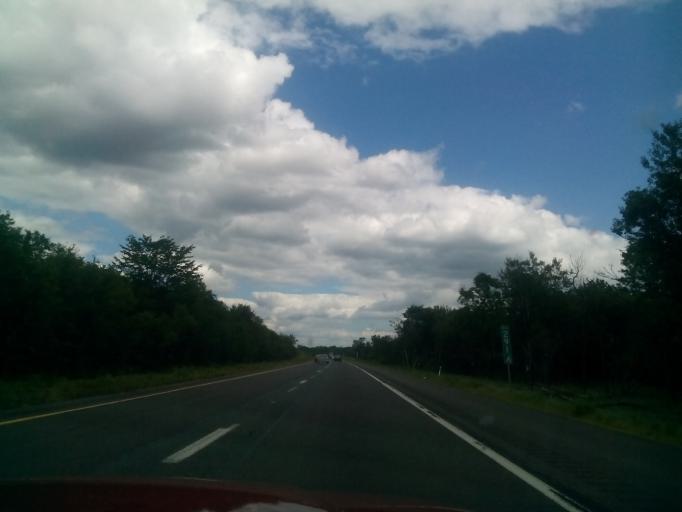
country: US
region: Pennsylvania
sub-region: Monroe County
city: Emerald Lakes
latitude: 41.0712
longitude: -75.4274
